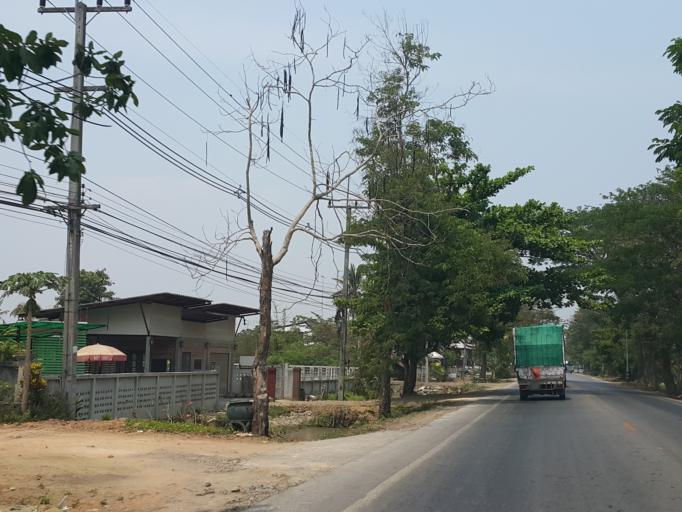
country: TH
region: Chiang Mai
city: Mae Taeng
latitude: 19.0286
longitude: 98.9673
